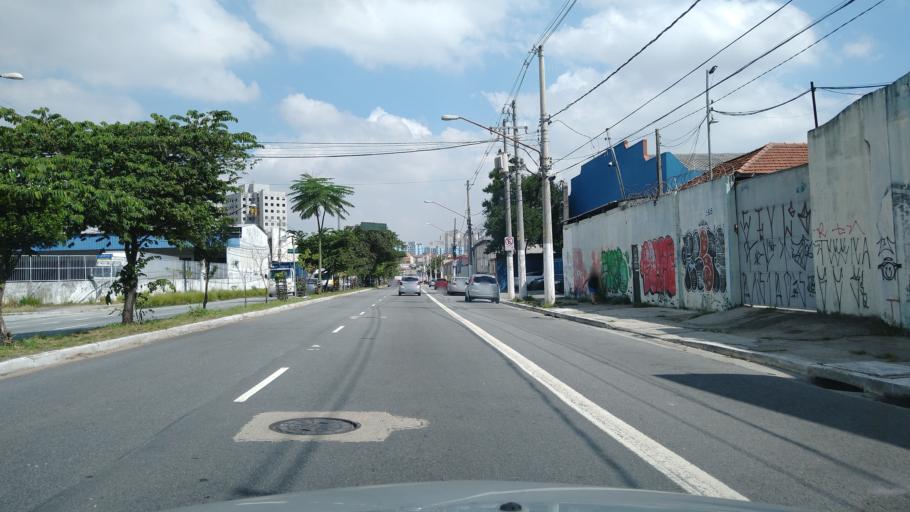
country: BR
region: Sao Paulo
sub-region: Guarulhos
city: Guarulhos
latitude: -23.4898
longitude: -46.5051
